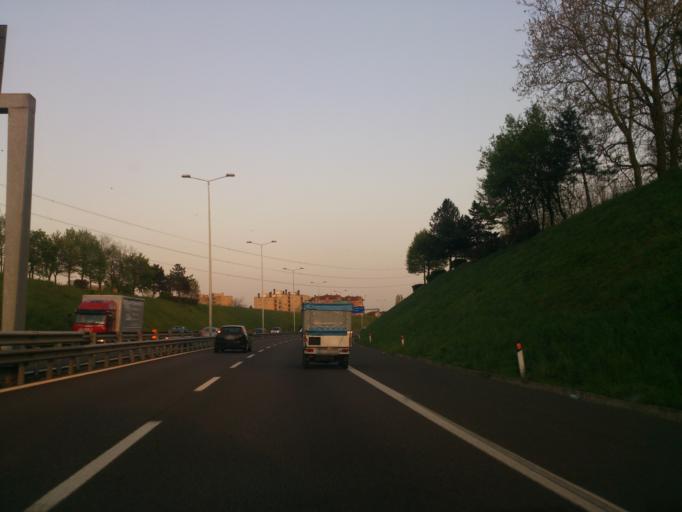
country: IT
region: Lombardy
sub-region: Provincia di Monza e Brianza
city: Muggio
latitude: 45.5764
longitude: 9.2188
